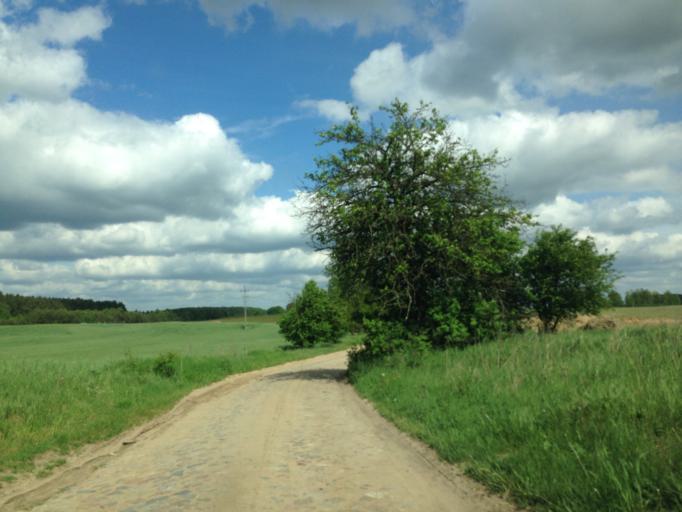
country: PL
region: Warmian-Masurian Voivodeship
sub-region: Powiat nidzicki
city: Kozlowo
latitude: 53.4390
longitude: 20.3021
